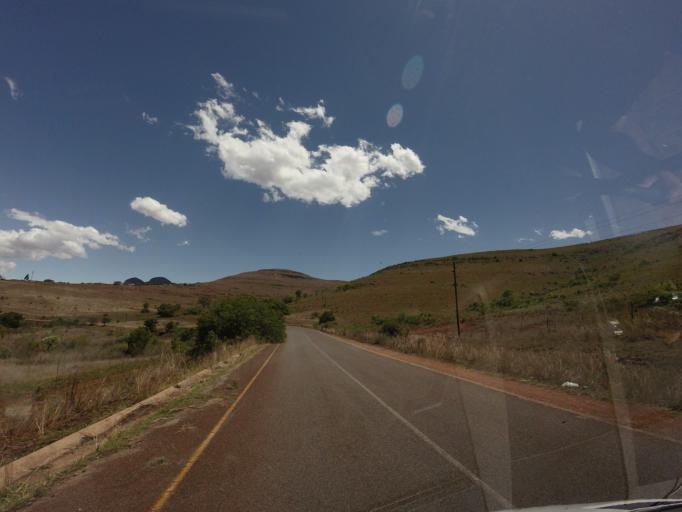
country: ZA
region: Limpopo
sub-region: Mopani District Municipality
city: Hoedspruit
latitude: -24.6053
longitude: 30.7878
